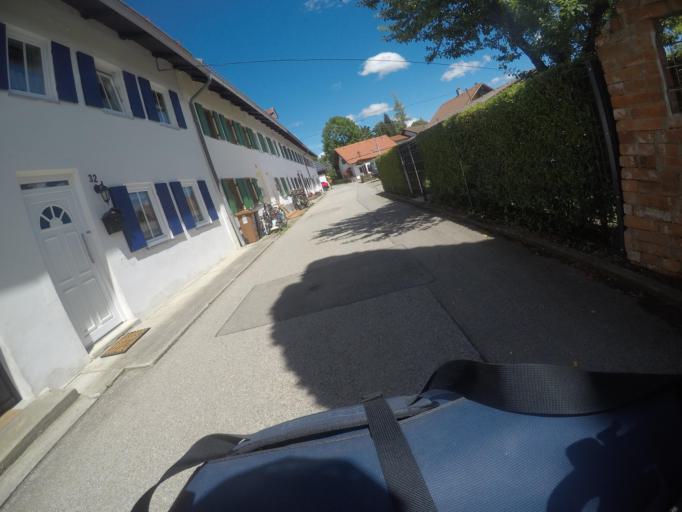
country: DE
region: Bavaria
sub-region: Swabia
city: Lechbruck
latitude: 47.6944
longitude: 10.7976
